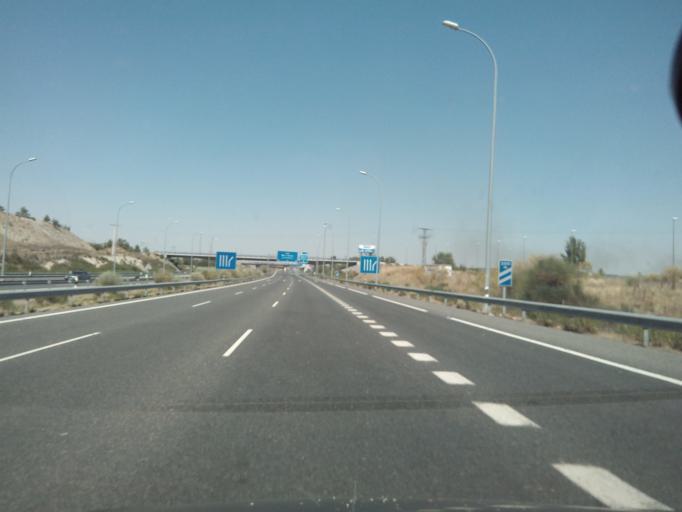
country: ES
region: Madrid
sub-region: Provincia de Madrid
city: Villa de Vallecas
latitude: 40.3526
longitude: -3.5747
